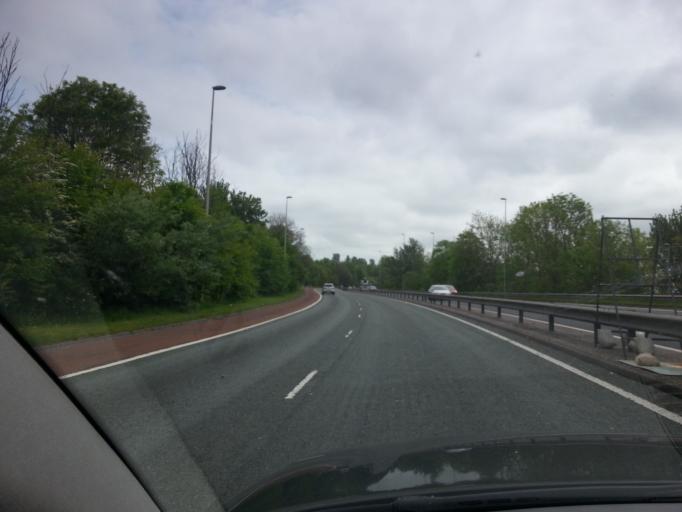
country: GB
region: England
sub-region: Cheshire West and Chester
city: Frodsham
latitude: 53.3172
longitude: -2.7367
